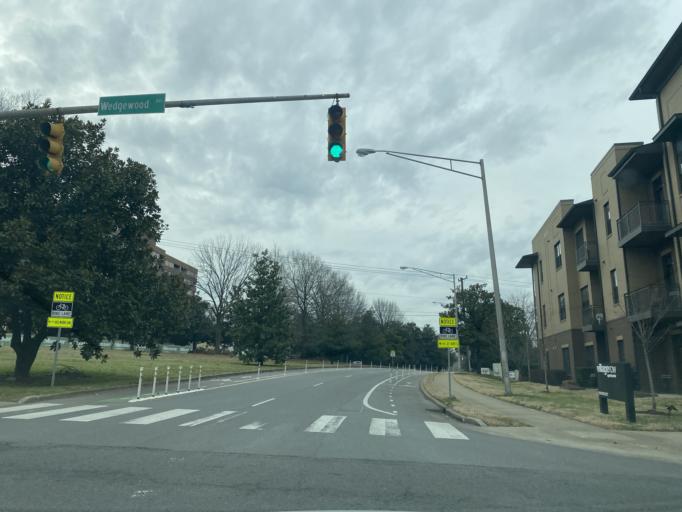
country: US
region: Tennessee
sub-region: Davidson County
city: Nashville
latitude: 36.1369
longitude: -86.7958
